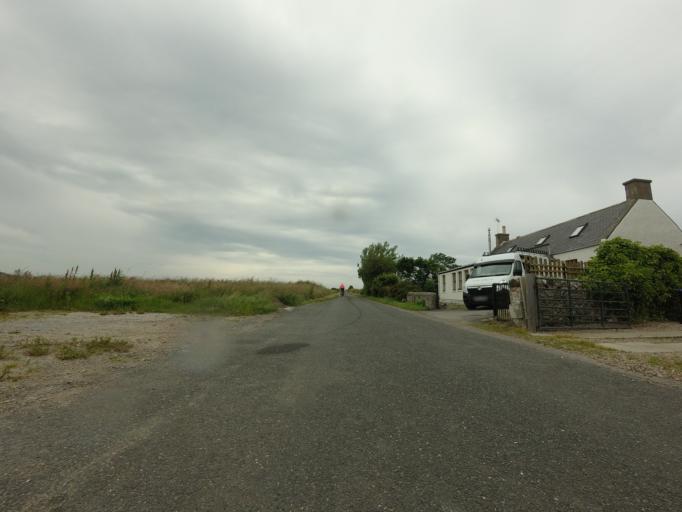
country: GB
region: Scotland
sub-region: Aberdeenshire
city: Portsoy
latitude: 57.6778
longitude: -2.6699
